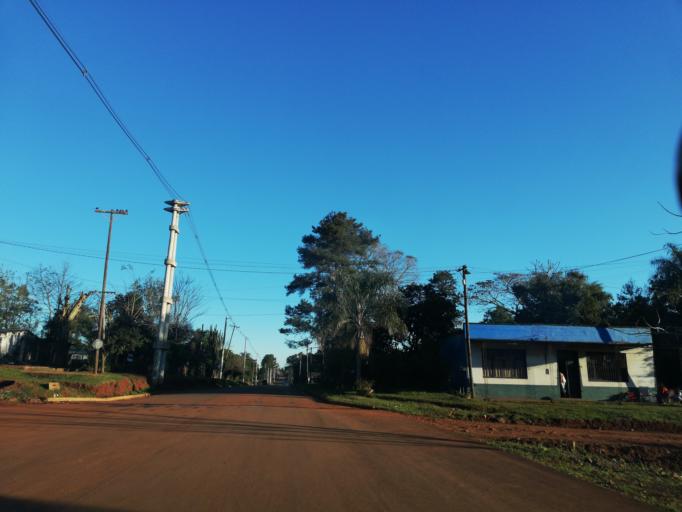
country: AR
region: Misiones
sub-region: Departamento de Candelaria
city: Candelaria
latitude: -27.4613
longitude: -55.7487
